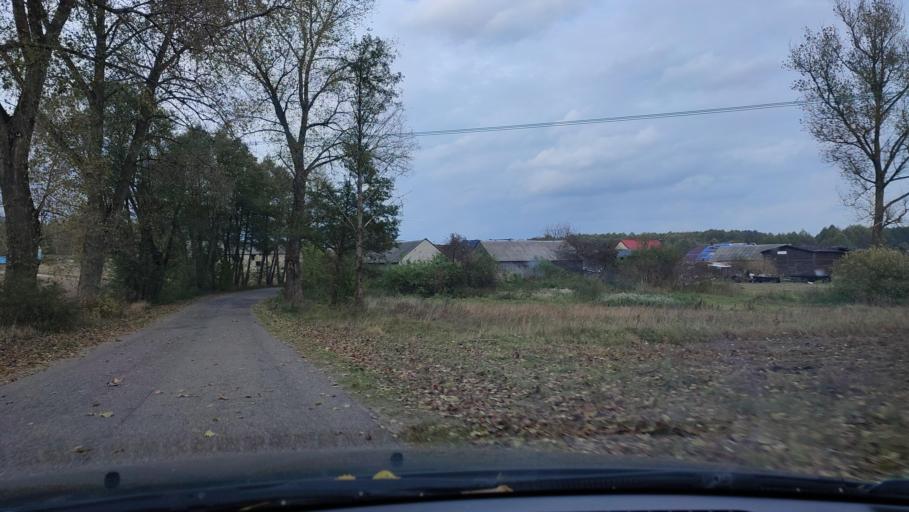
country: PL
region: Masovian Voivodeship
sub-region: Powiat mlawski
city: Mlawa
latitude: 53.1808
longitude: 20.3677
